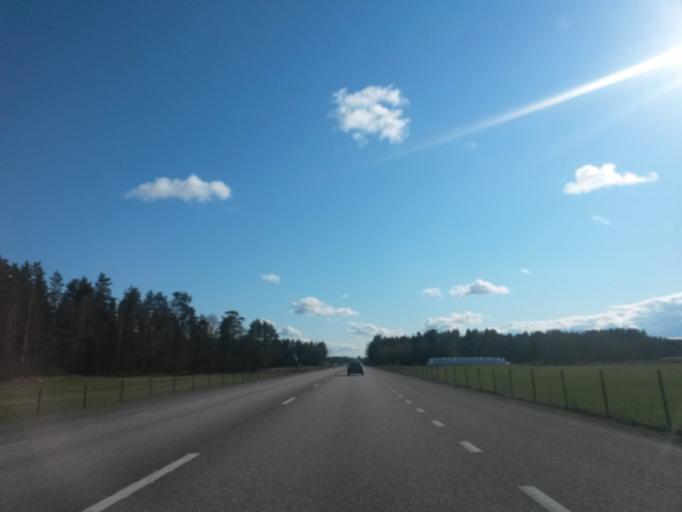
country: SE
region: Vaestra Goetaland
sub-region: Vara Kommun
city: Vara
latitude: 58.1794
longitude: 12.8943
